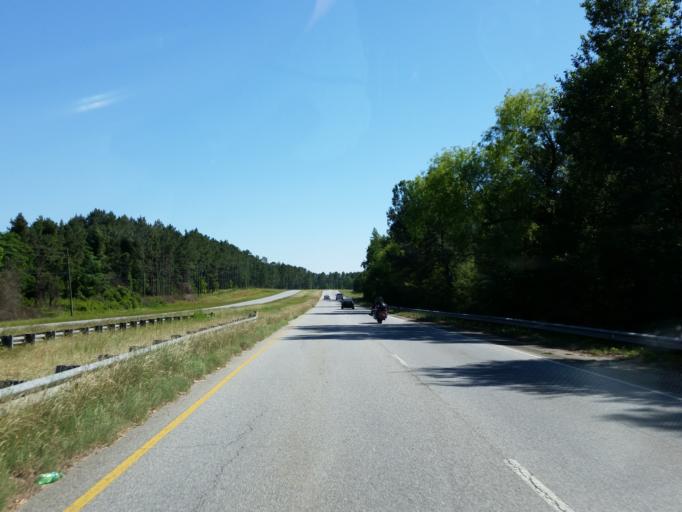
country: US
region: Georgia
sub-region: Lowndes County
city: Valdosta
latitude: 30.8042
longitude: -83.2355
